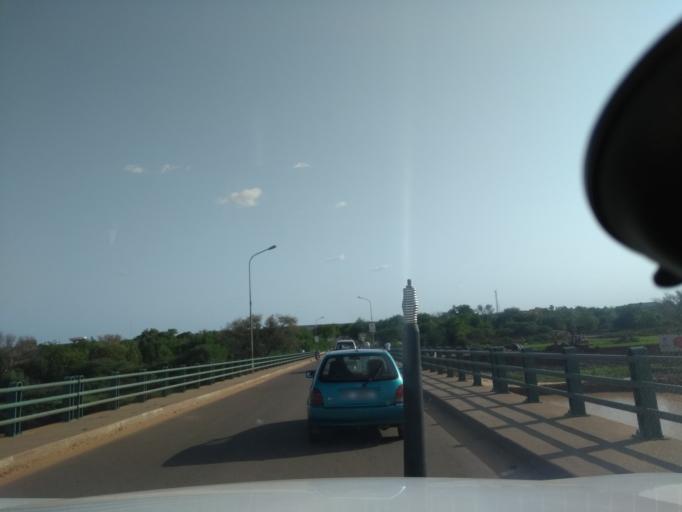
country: NE
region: Niamey
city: Niamey
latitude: 13.5038
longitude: 2.1030
